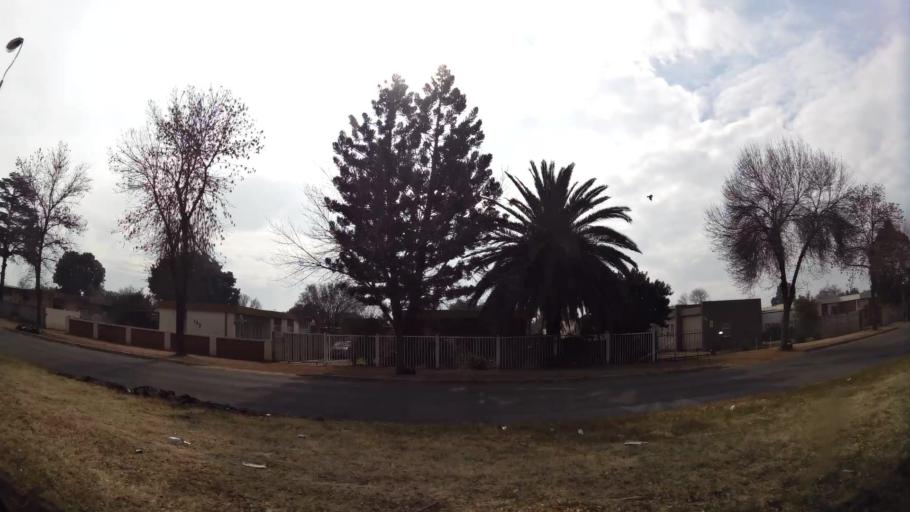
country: ZA
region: Gauteng
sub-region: Sedibeng District Municipality
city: Vanderbijlpark
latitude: -26.6868
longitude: 27.8424
